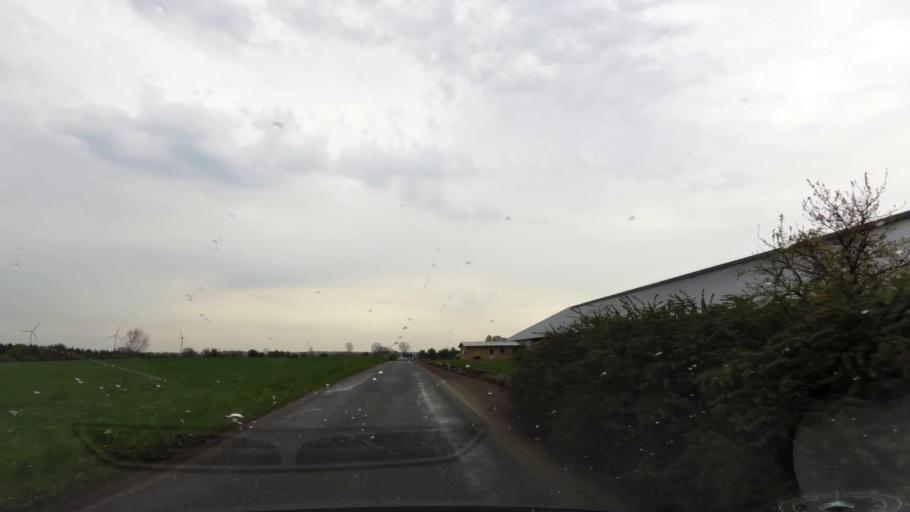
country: DK
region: South Denmark
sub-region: Svendborg Kommune
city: Svendborg
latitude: 55.1810
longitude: 10.5877
